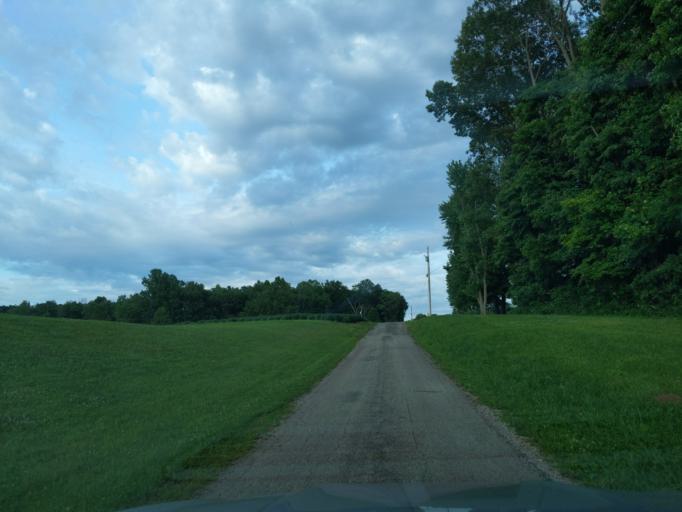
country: US
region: Indiana
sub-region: Ripley County
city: Sunman
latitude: 39.3101
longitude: -85.0962
